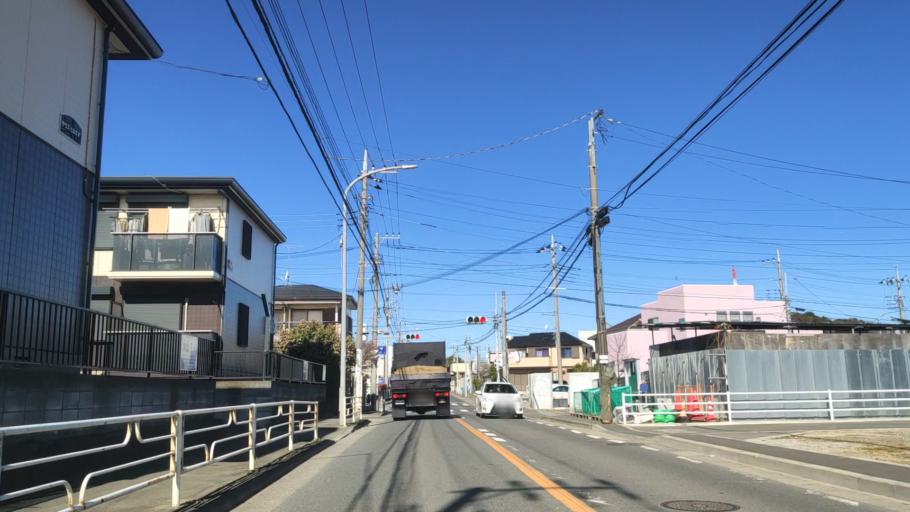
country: JP
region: Kanagawa
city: Minami-rinkan
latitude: 35.4951
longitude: 139.5165
